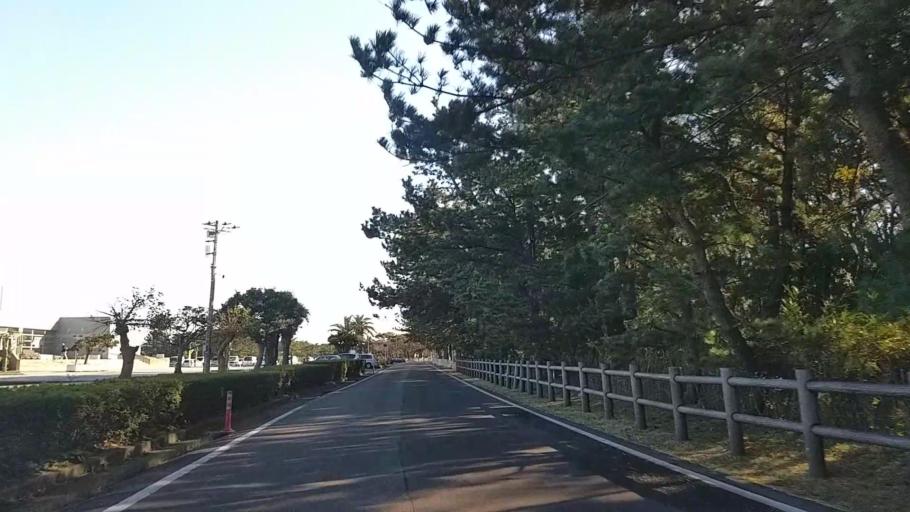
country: JP
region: Chiba
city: Futtsu
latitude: 35.3127
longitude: 139.8026
